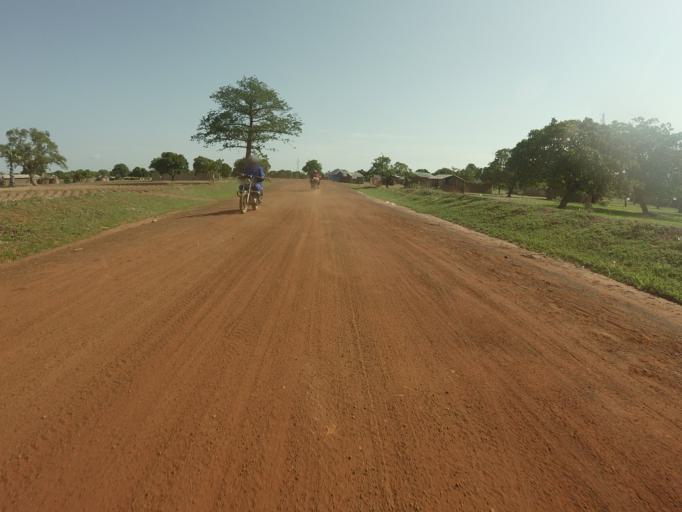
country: GH
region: Upper East
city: Bawku
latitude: 10.7803
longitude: -0.1906
